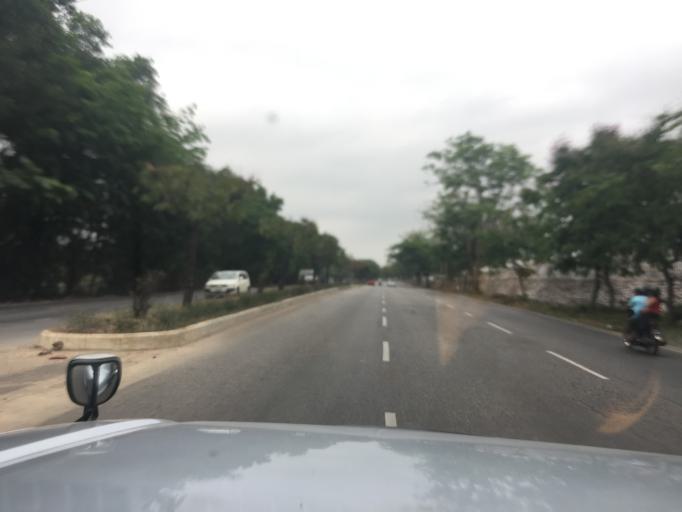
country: MM
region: Bago
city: Thanatpin
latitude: 17.1915
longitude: 96.3975
